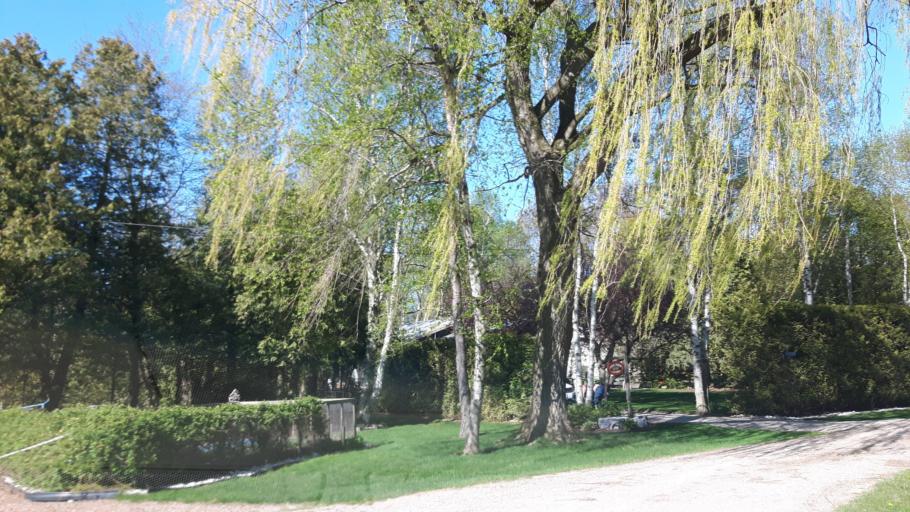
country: CA
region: Ontario
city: Bluewater
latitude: 43.5148
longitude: -81.7086
